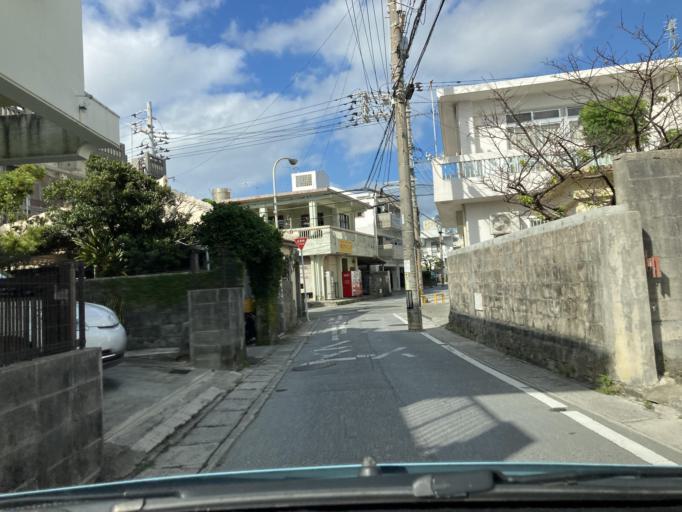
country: JP
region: Okinawa
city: Naha-shi
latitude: 26.2147
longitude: 127.7221
